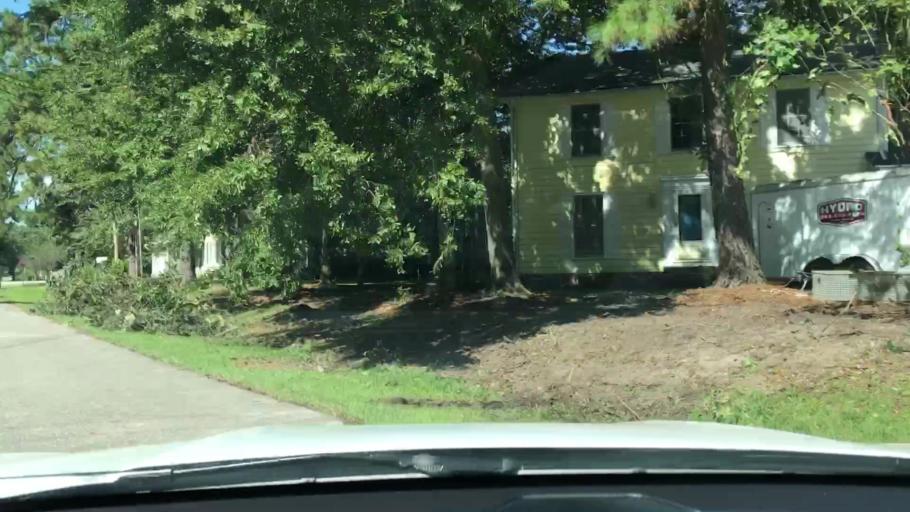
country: US
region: South Carolina
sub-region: Charleston County
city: Shell Point
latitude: 32.8467
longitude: -80.0603
